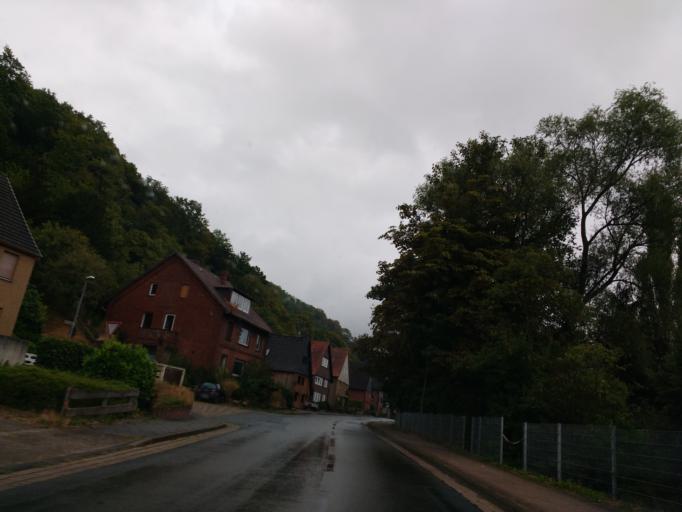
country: DE
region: Lower Saxony
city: Hameln
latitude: 52.0488
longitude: 9.4013
